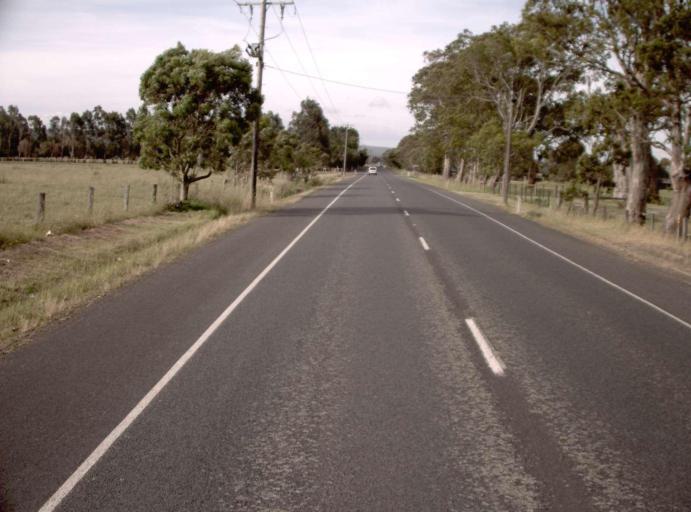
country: AU
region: Victoria
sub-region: Latrobe
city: Traralgon
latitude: -38.1423
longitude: 146.5563
